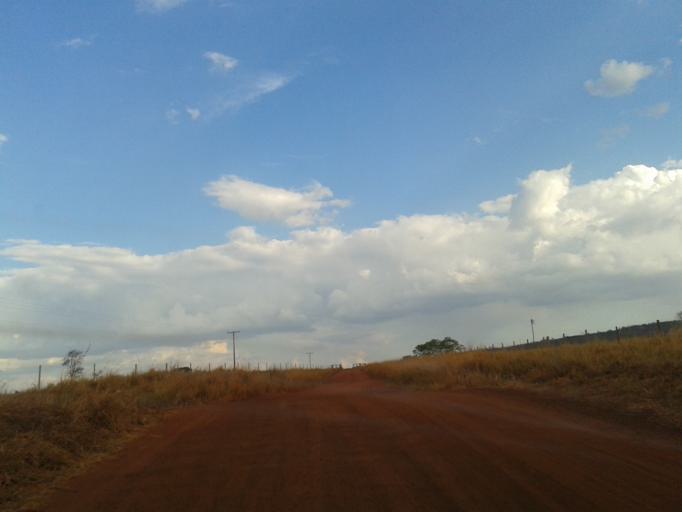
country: BR
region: Minas Gerais
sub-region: Ituiutaba
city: Ituiutaba
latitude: -19.1917
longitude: -49.8448
